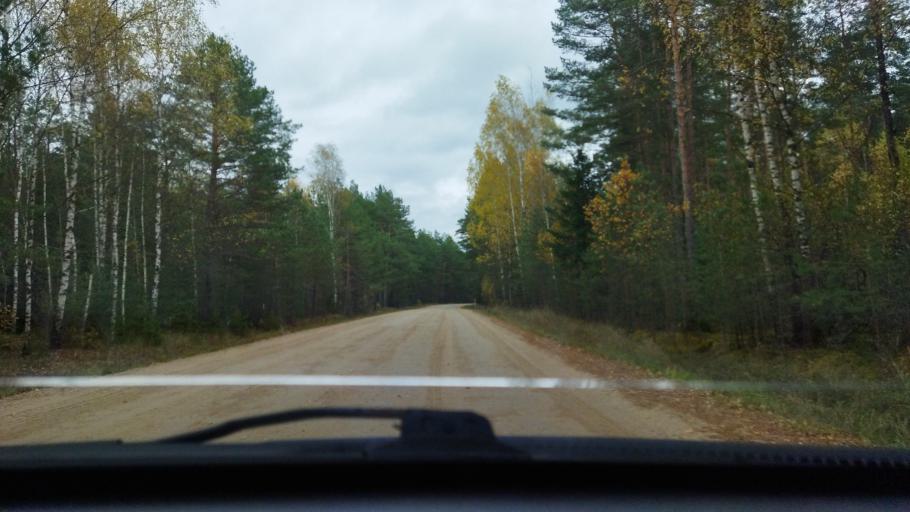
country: BY
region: Minsk
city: Svir
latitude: 54.8036
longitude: 26.2563
